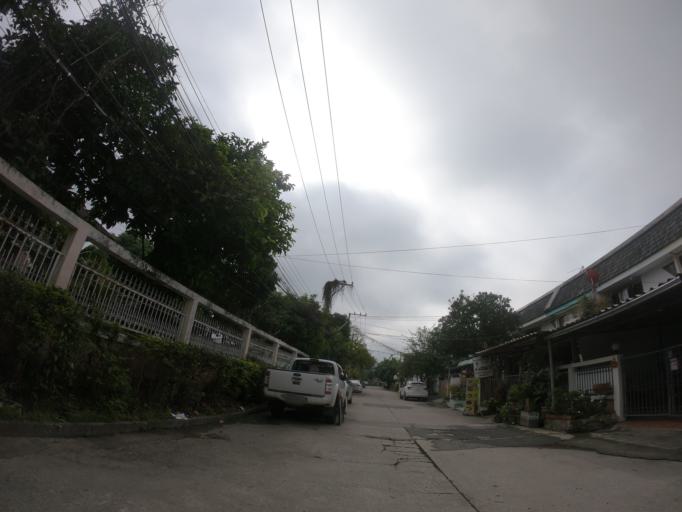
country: TH
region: Chiang Mai
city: Chiang Mai
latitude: 18.7600
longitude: 98.9768
